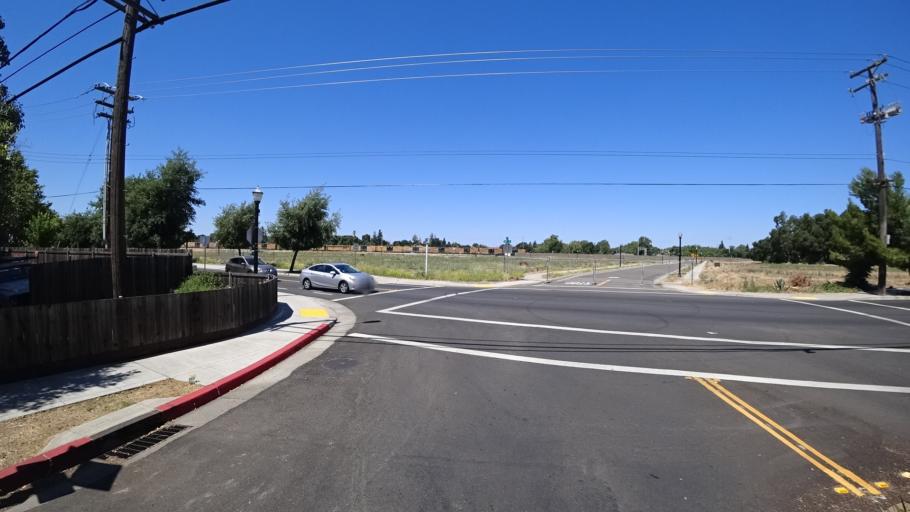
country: US
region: California
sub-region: Sacramento County
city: Sacramento
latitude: 38.5489
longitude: -121.4834
